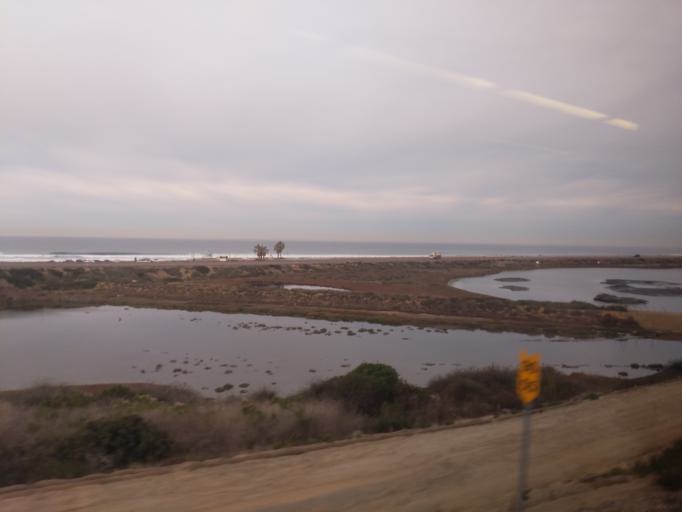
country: US
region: California
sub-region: San Diego County
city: Solana Beach
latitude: 33.0024
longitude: -117.2754
